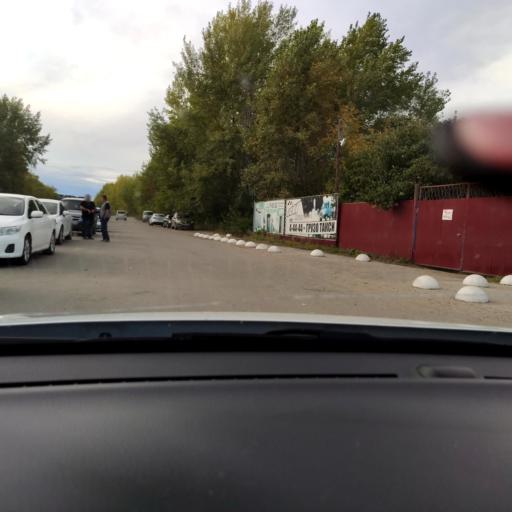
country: RU
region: Tatarstan
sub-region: Zelenodol'skiy Rayon
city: Zelenodolsk
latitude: 55.8258
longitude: 48.5240
